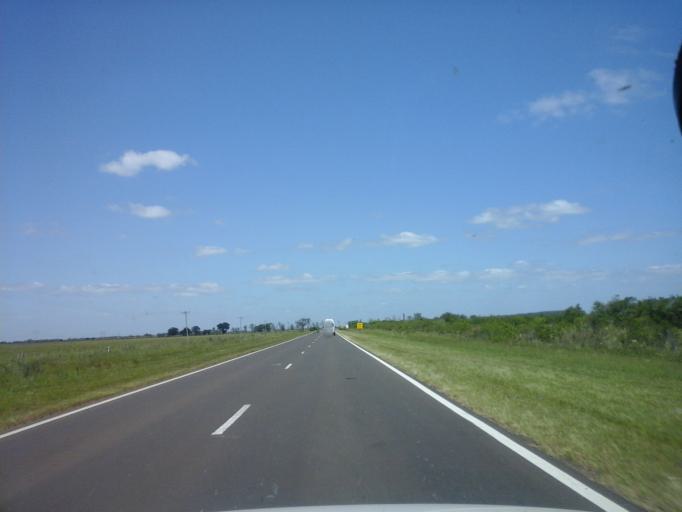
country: AR
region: Corrientes
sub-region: Departamento de Itati
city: Itati
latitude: -27.3196
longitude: -57.9999
